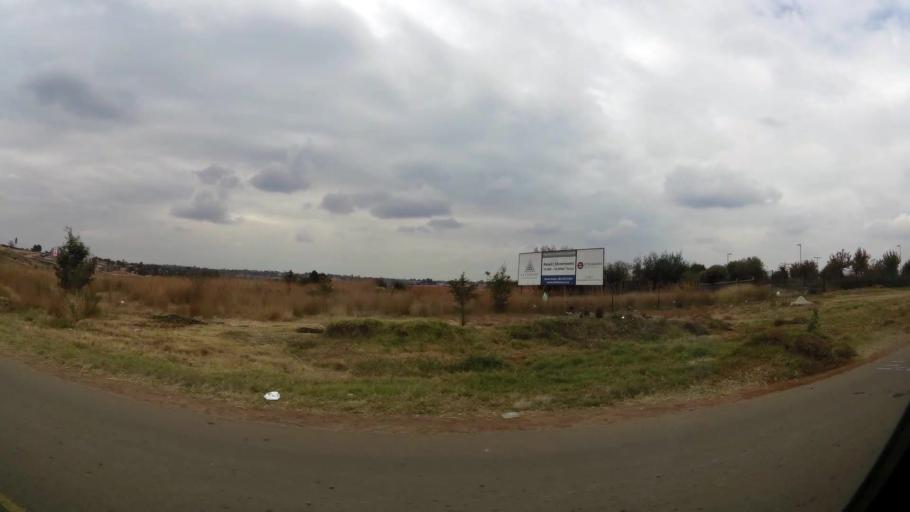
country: ZA
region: Gauteng
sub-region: City of Johannesburg Metropolitan Municipality
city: Roodepoort
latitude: -26.1090
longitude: 27.8839
